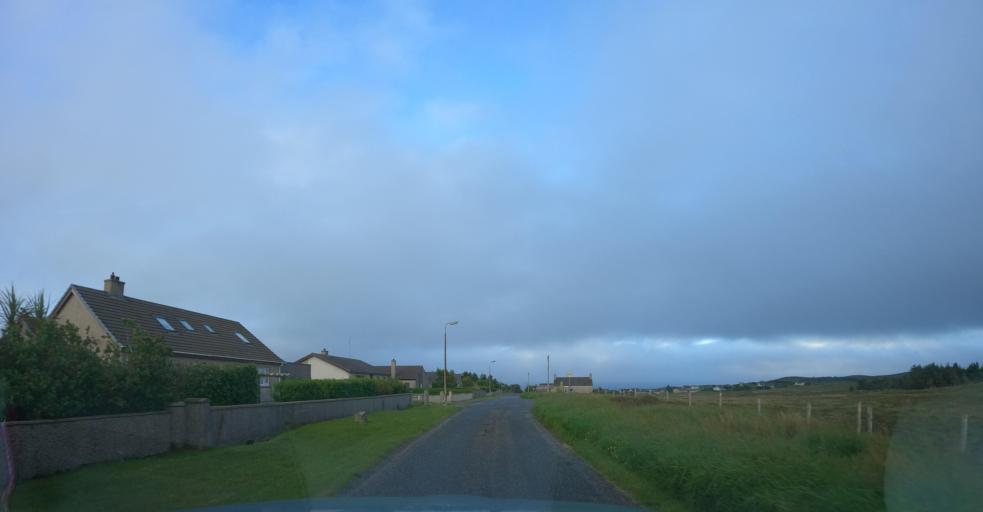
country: GB
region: Scotland
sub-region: Eilean Siar
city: Stornoway
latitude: 58.2019
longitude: -6.2314
